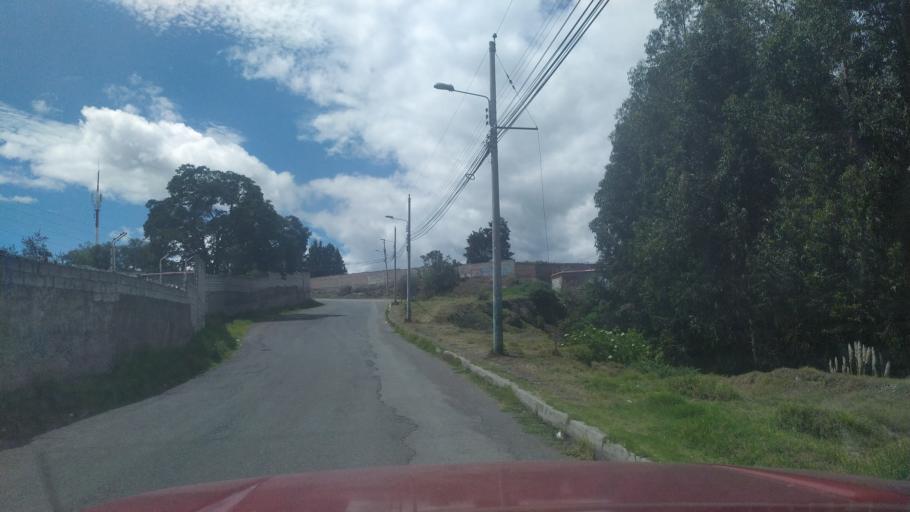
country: EC
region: Chimborazo
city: Riobamba
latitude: -1.6713
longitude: -78.6674
